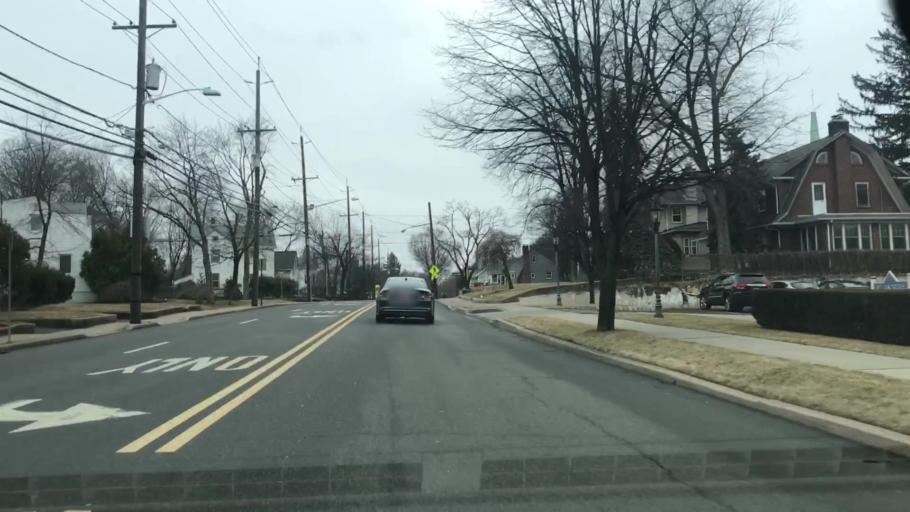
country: US
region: New Jersey
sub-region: Bergen County
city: Westwood
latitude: 40.9924
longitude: -74.0369
